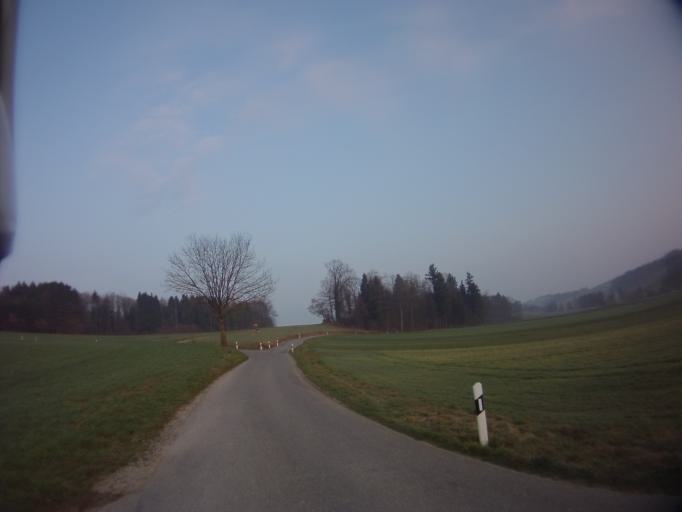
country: CH
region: Zurich
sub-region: Bezirk Affoltern
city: Knonau
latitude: 47.2184
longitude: 8.4489
